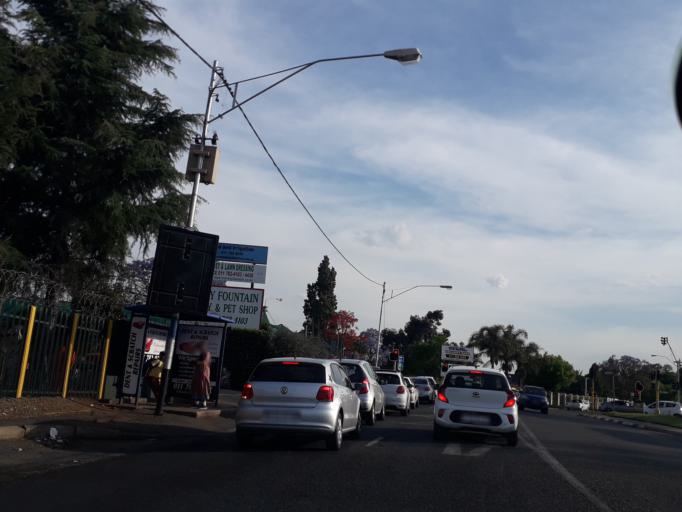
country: ZA
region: Gauteng
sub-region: City of Johannesburg Metropolitan Municipality
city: Johannesburg
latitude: -26.1262
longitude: 27.9964
